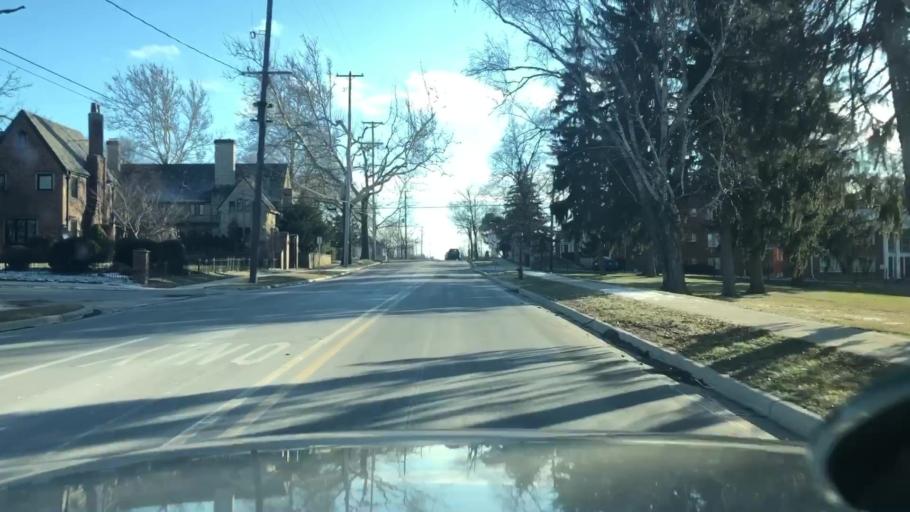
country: US
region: Michigan
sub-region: Jackson County
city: Jackson
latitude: 42.2298
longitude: -84.4232
